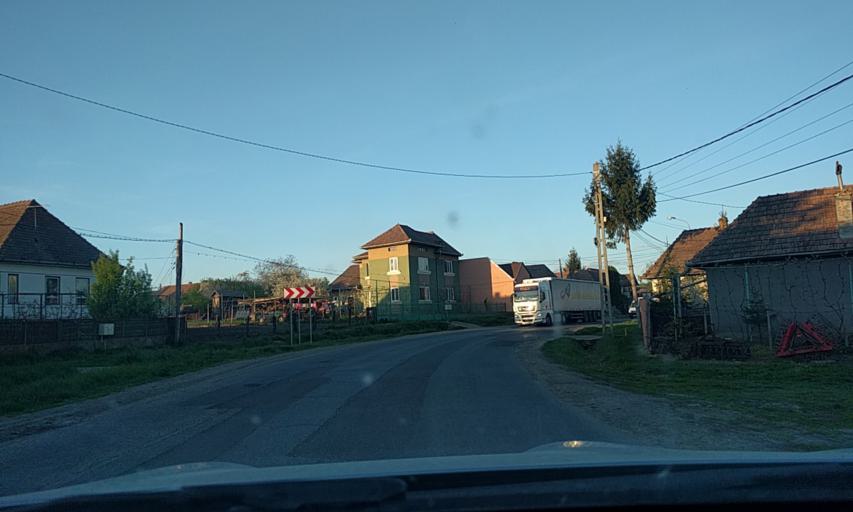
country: RO
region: Mures
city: Gheorghe Doja
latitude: 46.4714
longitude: 24.4895
